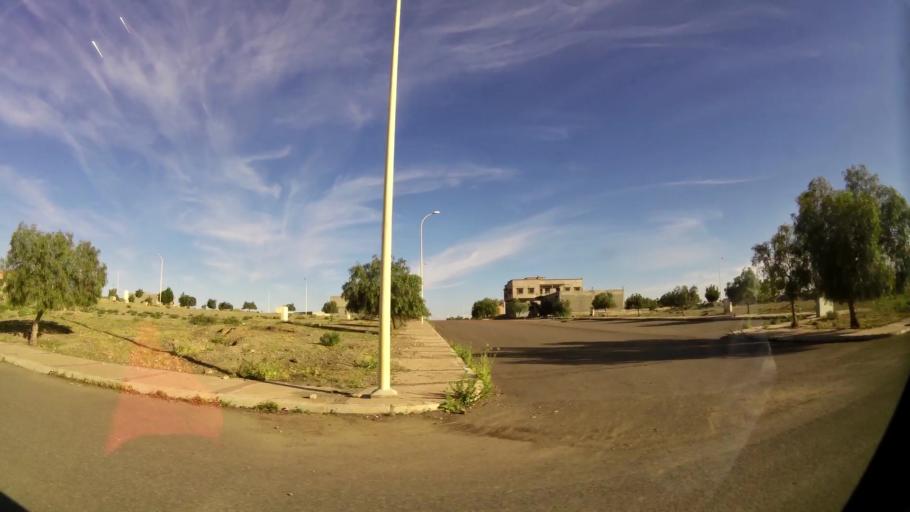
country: MA
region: Marrakech-Tensift-Al Haouz
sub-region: Marrakech
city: Marrakesh
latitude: 31.7600
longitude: -8.0960
